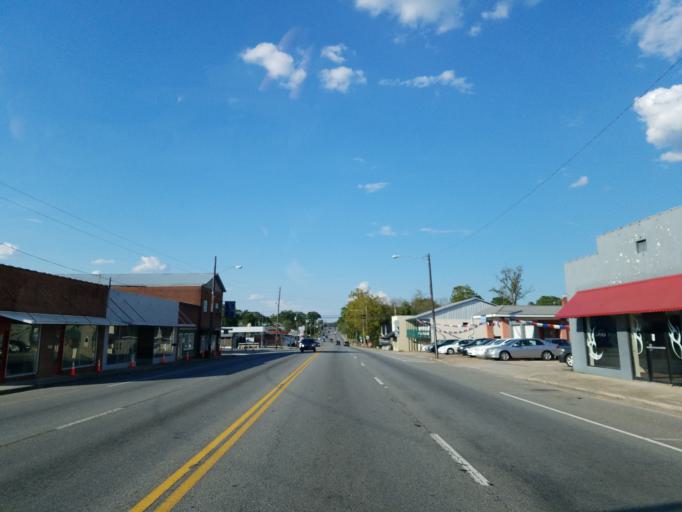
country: US
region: Georgia
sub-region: Murray County
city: Chatsworth
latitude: 34.7678
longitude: -84.7696
